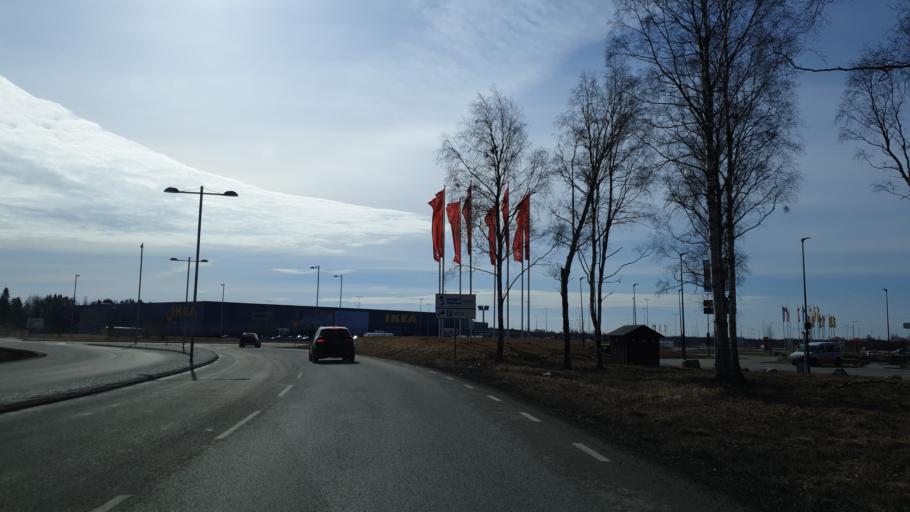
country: SE
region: Vaesterbotten
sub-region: Umea Kommun
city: Umea
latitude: 63.8109
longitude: 20.2509
